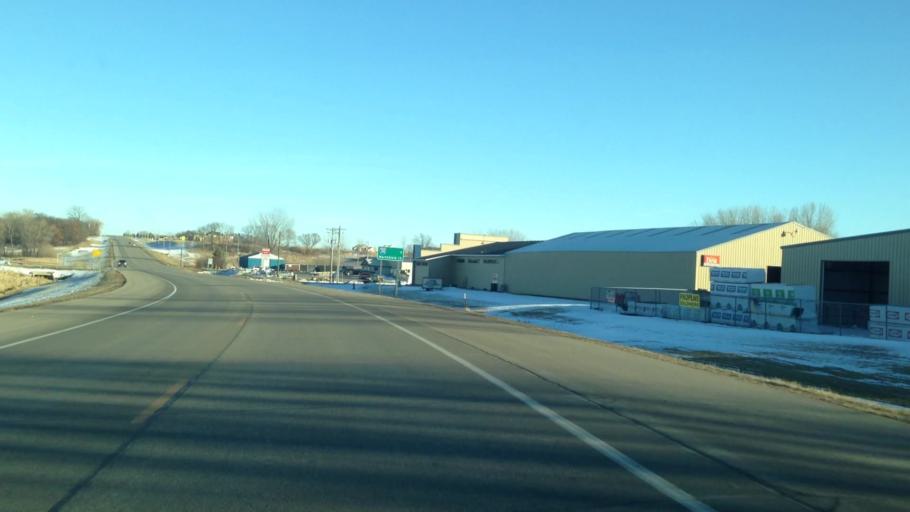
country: US
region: Minnesota
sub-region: Rice County
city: Lonsdale
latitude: 44.4792
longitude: -93.4200
